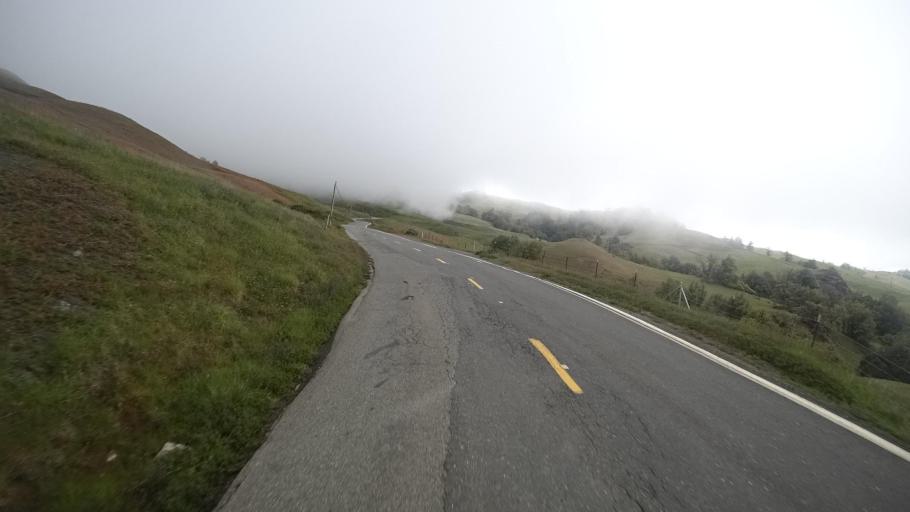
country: US
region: California
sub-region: Humboldt County
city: Redway
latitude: 40.1057
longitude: -123.7022
